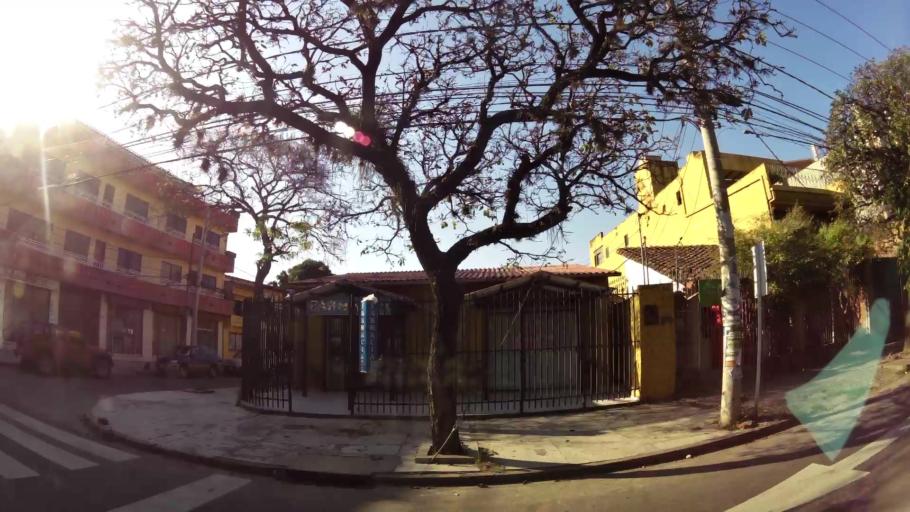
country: BO
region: Santa Cruz
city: Santa Cruz de la Sierra
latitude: -17.7834
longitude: -63.1928
